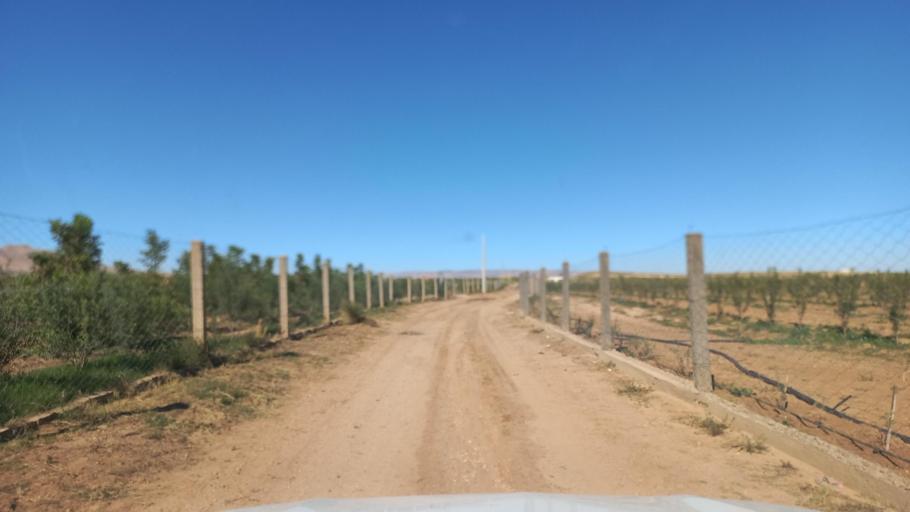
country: TN
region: Al Qasrayn
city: Sbiba
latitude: 35.3919
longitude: 9.0823
